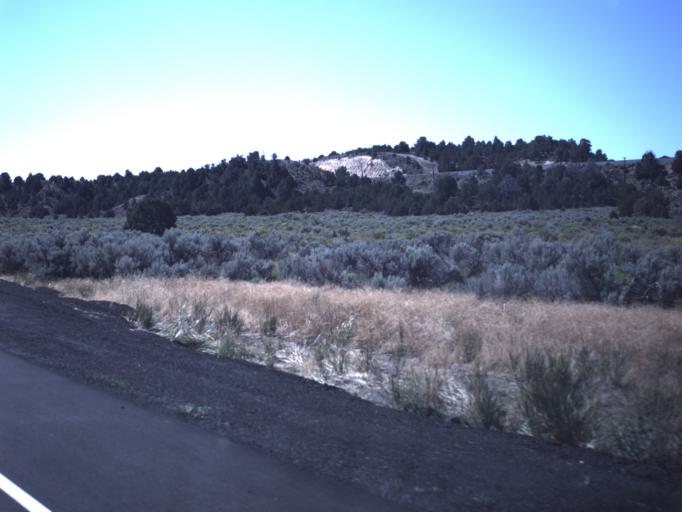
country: US
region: Utah
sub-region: Utah County
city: Eagle Mountain
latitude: 39.9934
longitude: -112.2694
